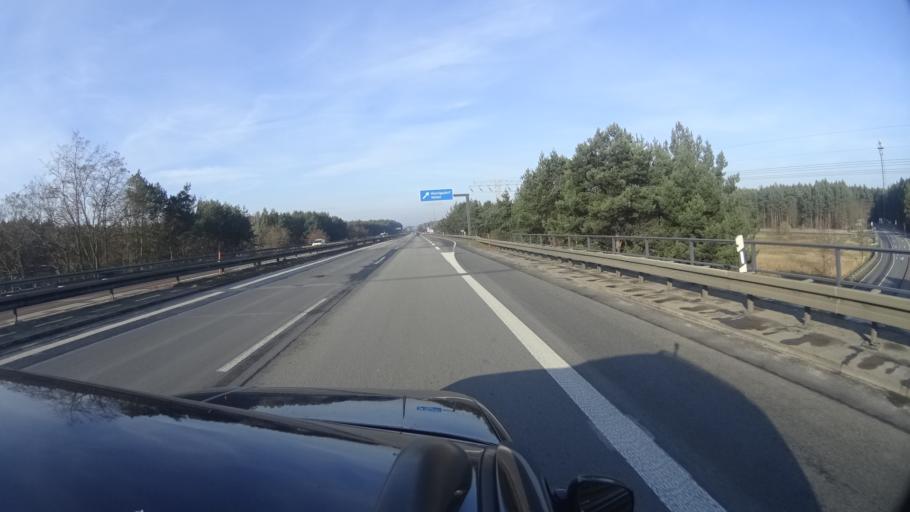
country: DE
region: Brandenburg
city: Hennigsdorf
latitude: 52.6762
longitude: 13.2293
